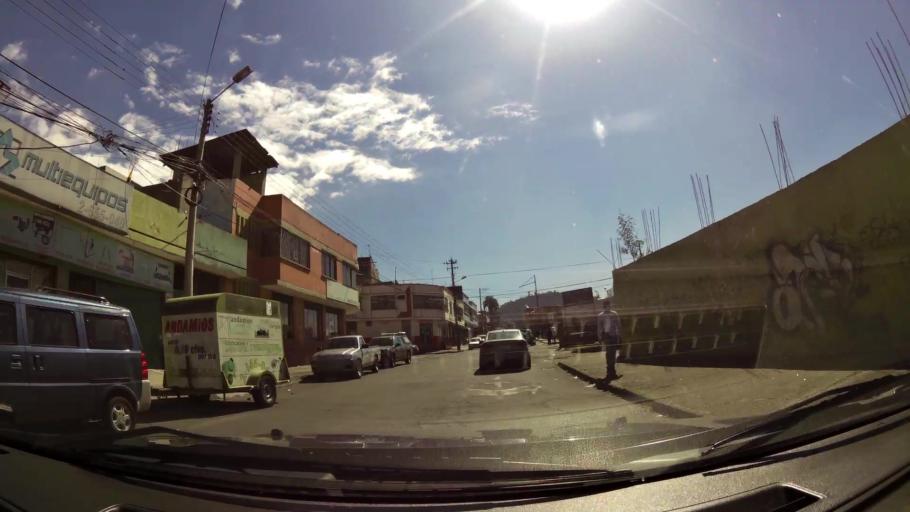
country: EC
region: Pichincha
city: Quito
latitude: -0.2420
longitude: -78.5305
